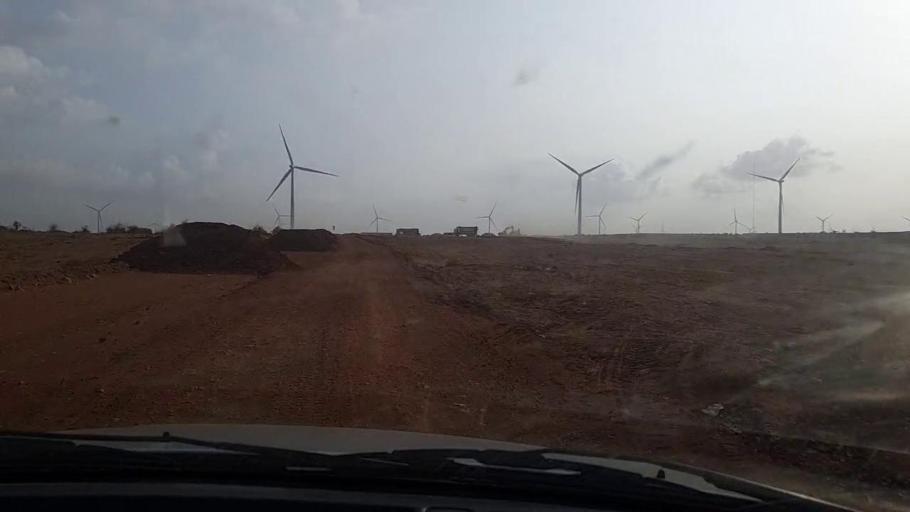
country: PK
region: Sindh
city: Thatta
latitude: 25.0491
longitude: 67.8677
